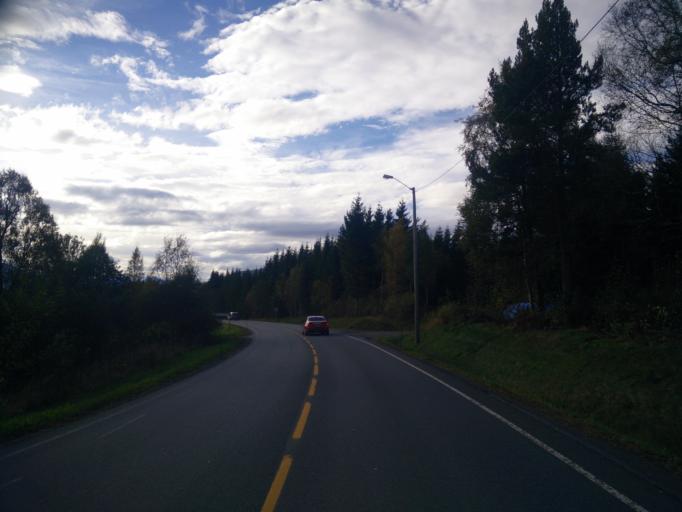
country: NO
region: More og Romsdal
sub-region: Vestnes
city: Vestnes
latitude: 62.6466
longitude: 7.0816
